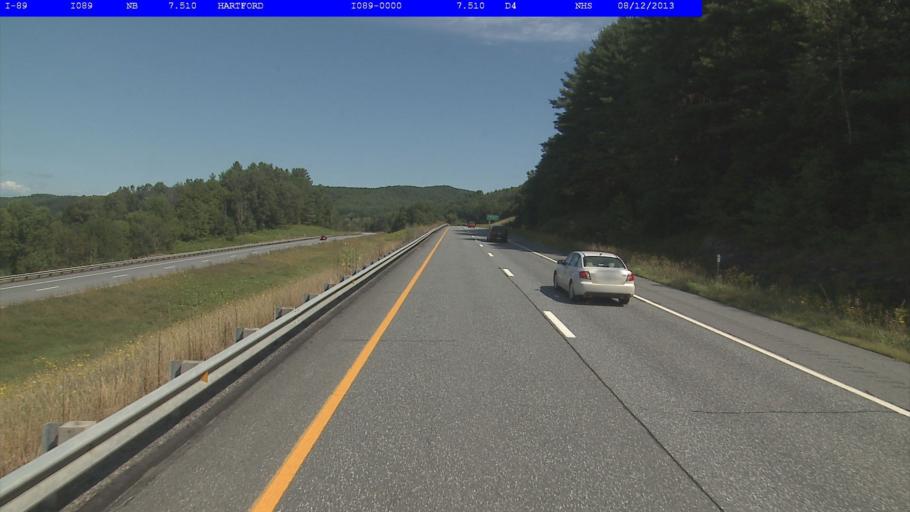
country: US
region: Vermont
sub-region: Windsor County
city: Wilder
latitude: 43.7130
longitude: -72.4132
